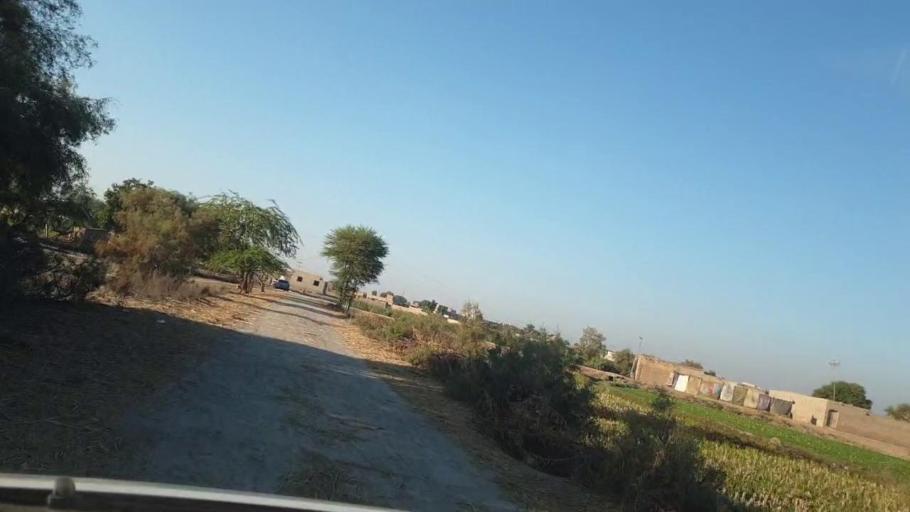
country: PK
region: Sindh
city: Khairpur Nathan Shah
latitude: 27.0437
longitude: 67.7267
